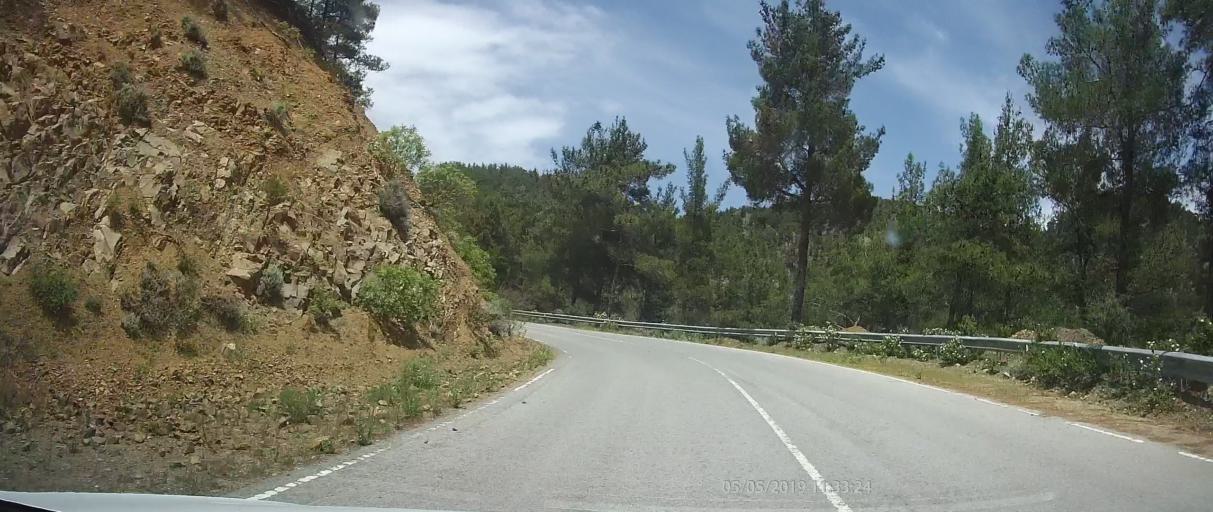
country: CY
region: Lefkosia
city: Kato Pyrgos
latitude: 34.9609
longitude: 32.6473
